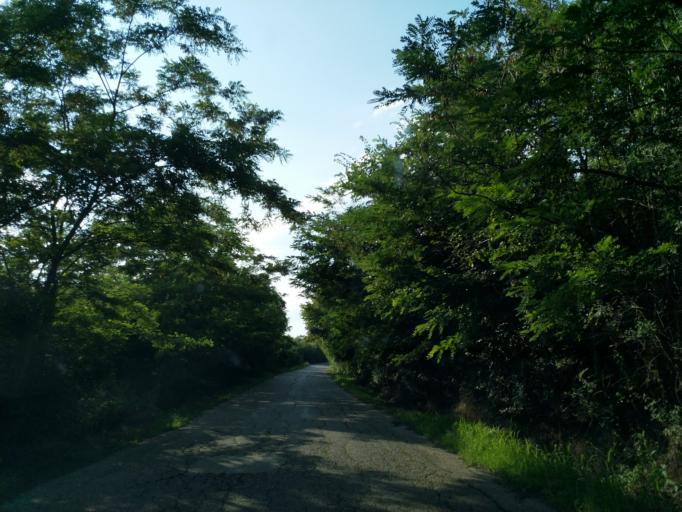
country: RS
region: Central Serbia
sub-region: Pomoravski Okrug
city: Jagodina
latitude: 43.9958
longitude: 21.1942
